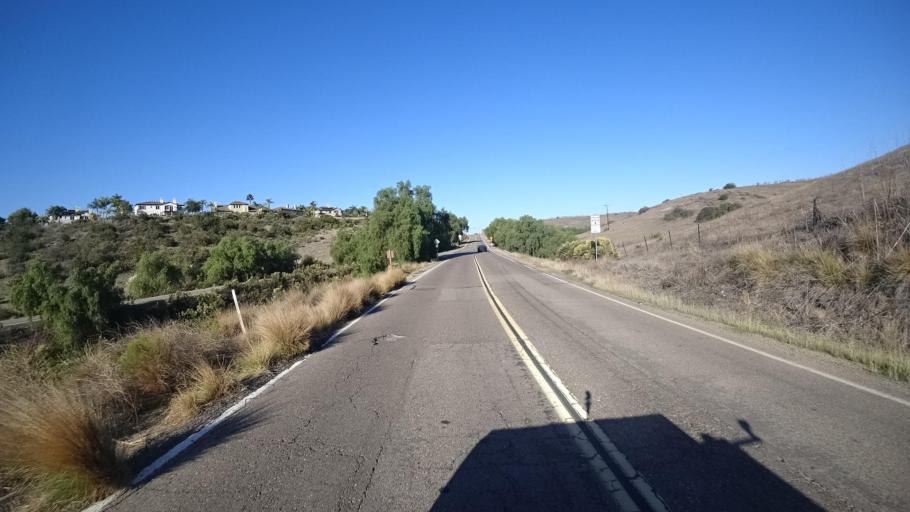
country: US
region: California
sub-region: San Diego County
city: La Presa
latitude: 32.6431
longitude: -116.9352
